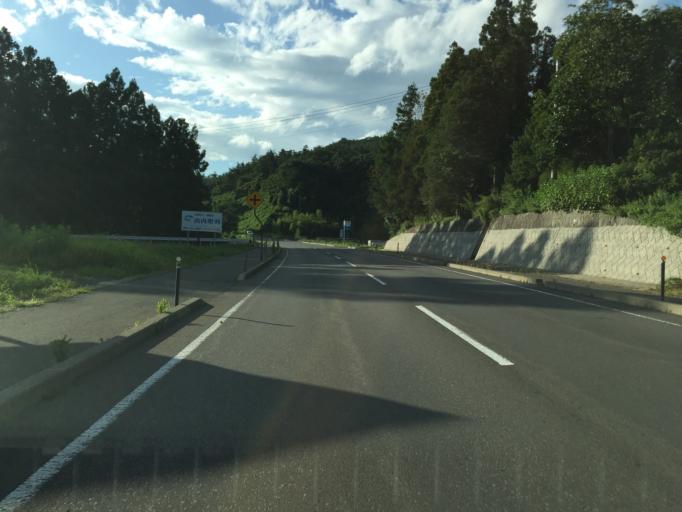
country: JP
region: Fukushima
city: Fukushima-shi
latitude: 37.7210
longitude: 140.4981
